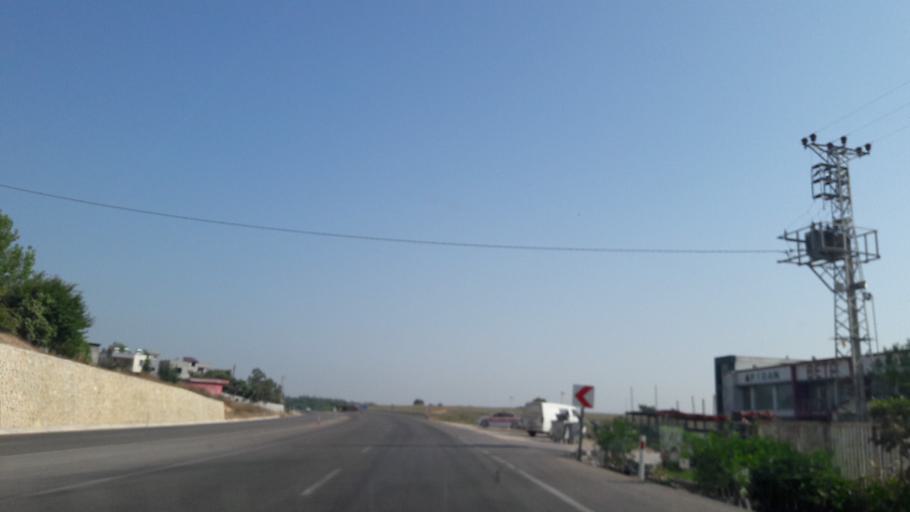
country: TR
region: Adana
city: Sagkaya
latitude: 37.1428
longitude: 35.5397
